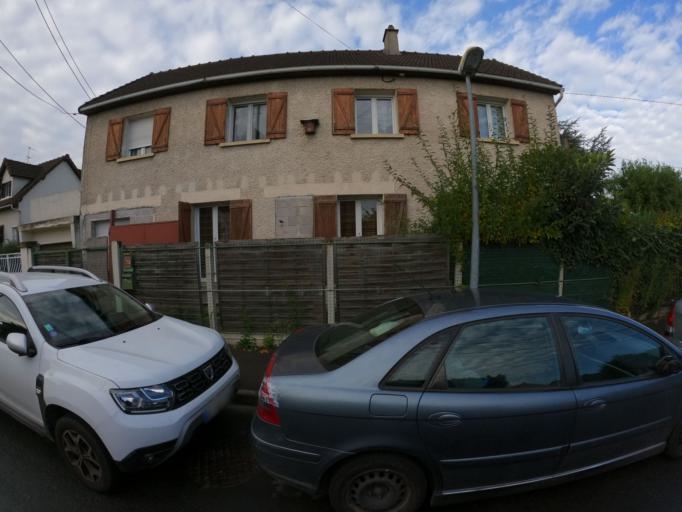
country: FR
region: Ile-de-France
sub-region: Departement de Seine-et-Marne
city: Courtry
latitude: 48.9031
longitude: 2.6058
